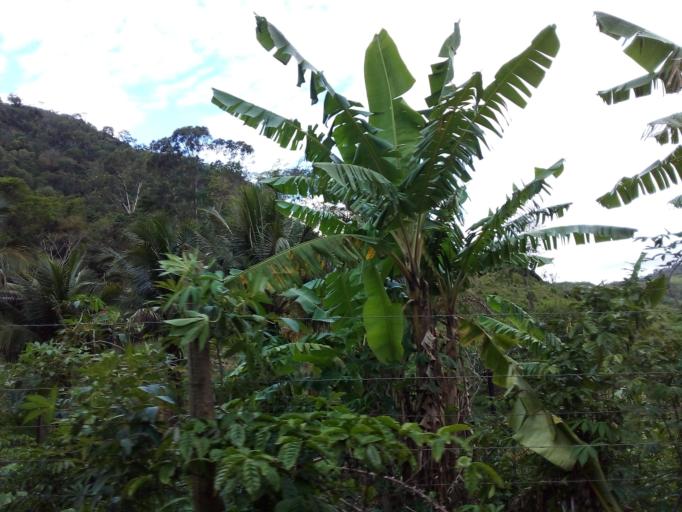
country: BR
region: Espirito Santo
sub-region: Joao Neiva
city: Joao Neiva
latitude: -19.7504
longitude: -40.3664
